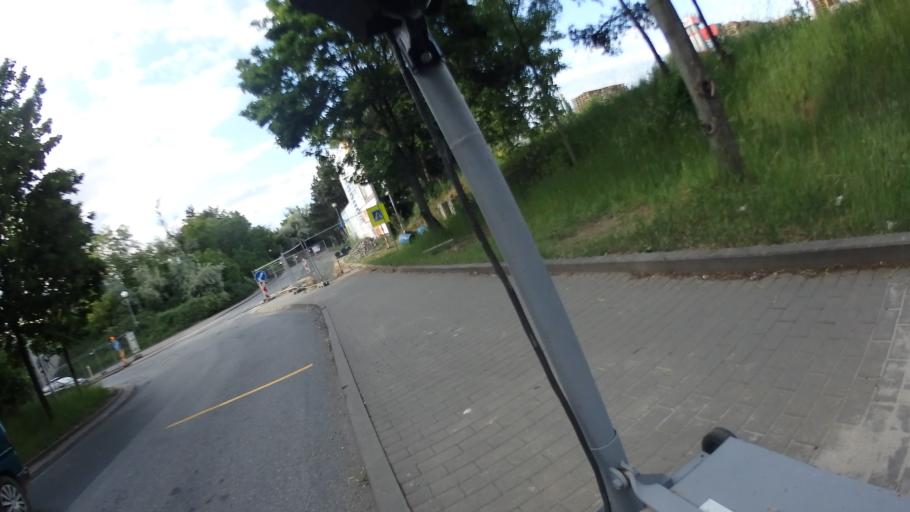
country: CZ
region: South Moravian
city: Moravany
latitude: 49.1572
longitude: 16.6008
